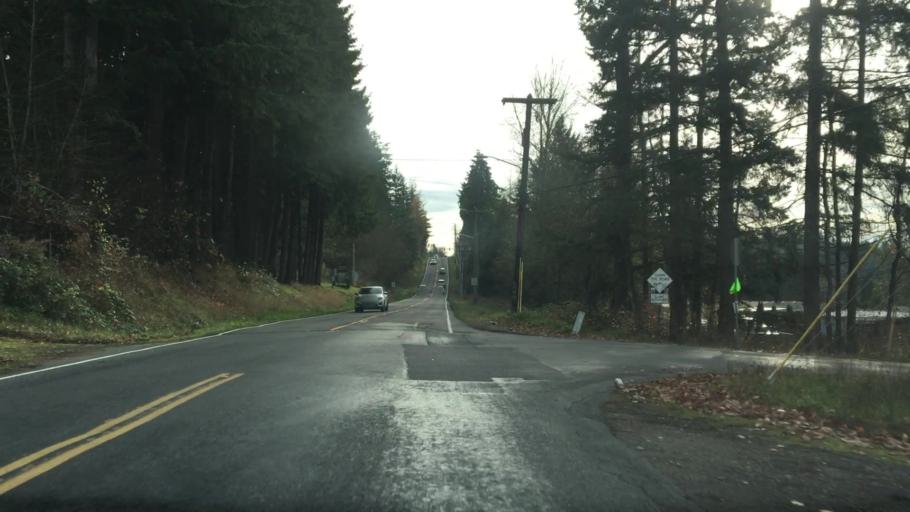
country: US
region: Washington
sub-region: Pierce County
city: Frederickson
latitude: 47.1151
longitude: -122.3255
